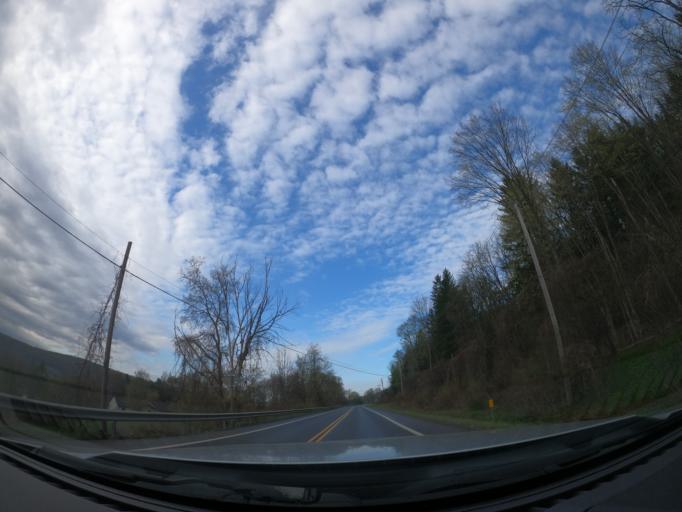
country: US
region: New York
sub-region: Cortland County
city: Homer
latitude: 42.6436
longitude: -76.1317
